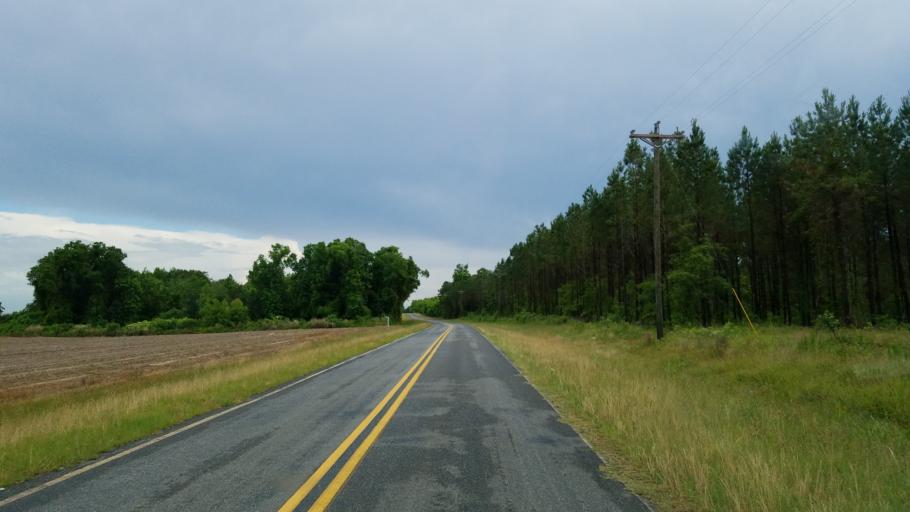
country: US
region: Georgia
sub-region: Dooly County
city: Unadilla
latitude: 32.2064
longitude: -83.7981
